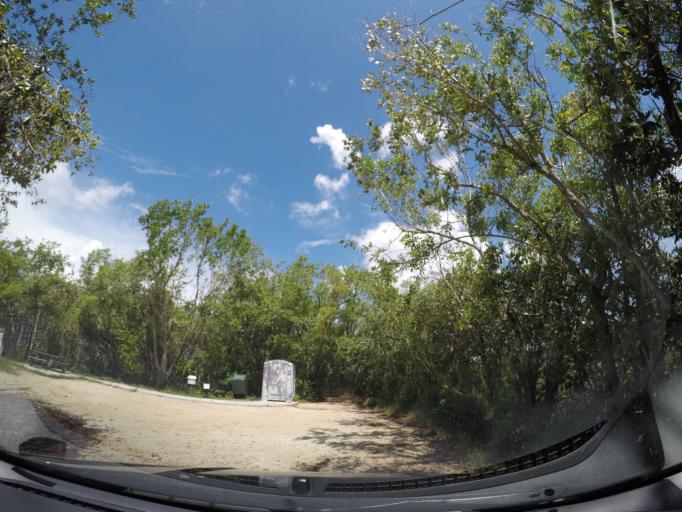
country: US
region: Florida
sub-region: Collier County
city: Marco
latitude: 25.9315
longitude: -81.4443
